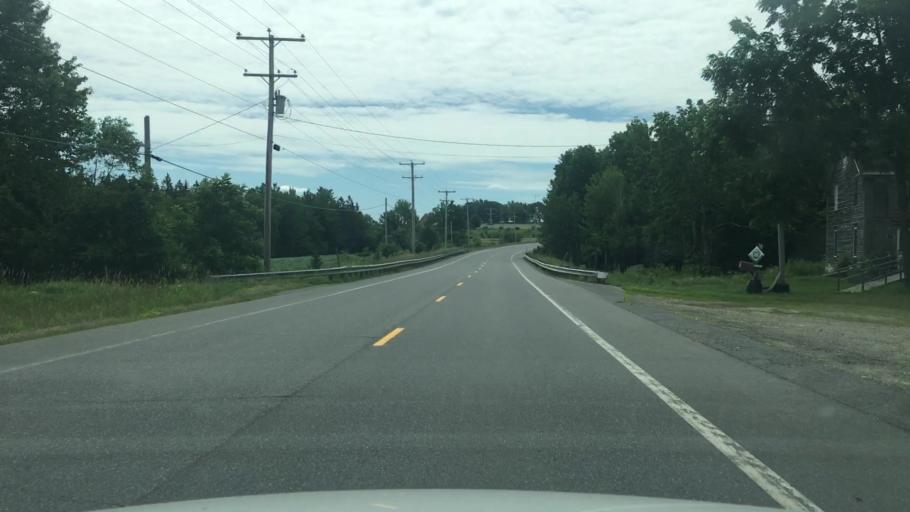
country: US
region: Maine
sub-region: Waldo County
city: Troy
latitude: 44.5482
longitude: -69.2667
